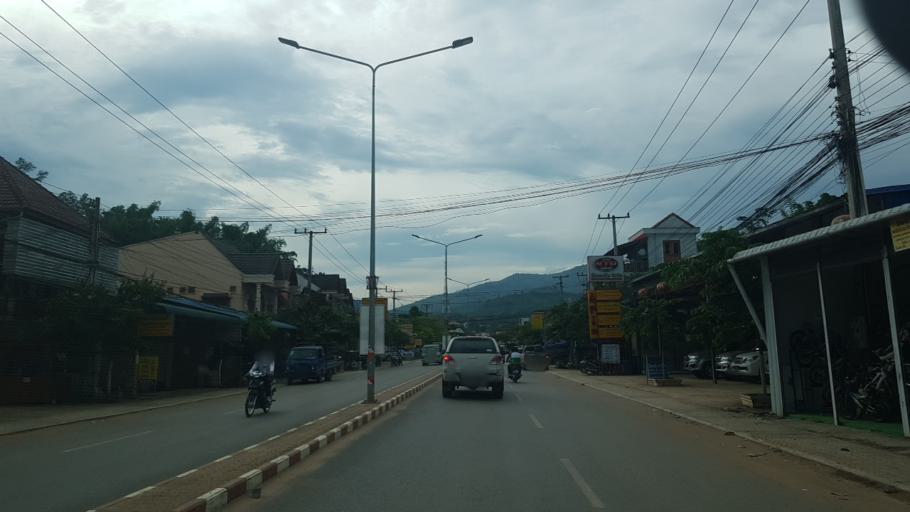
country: LA
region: Oudomxai
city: Muang Xay
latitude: 20.6862
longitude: 101.9874
